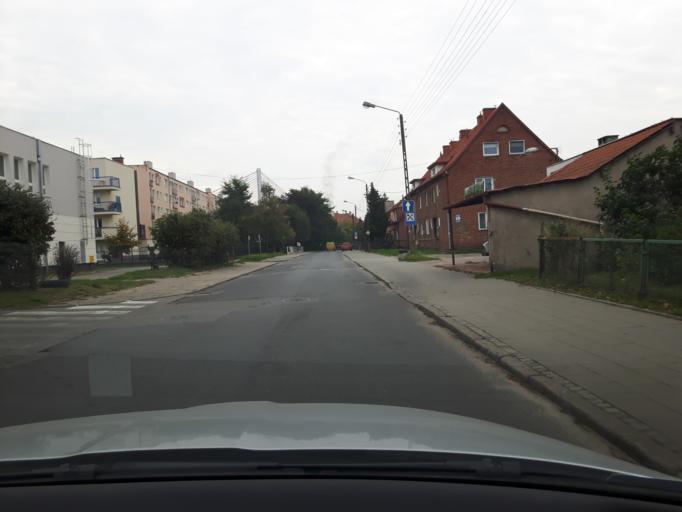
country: PL
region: Pomeranian Voivodeship
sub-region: Gdansk
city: Gdansk
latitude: 54.3560
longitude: 18.6844
